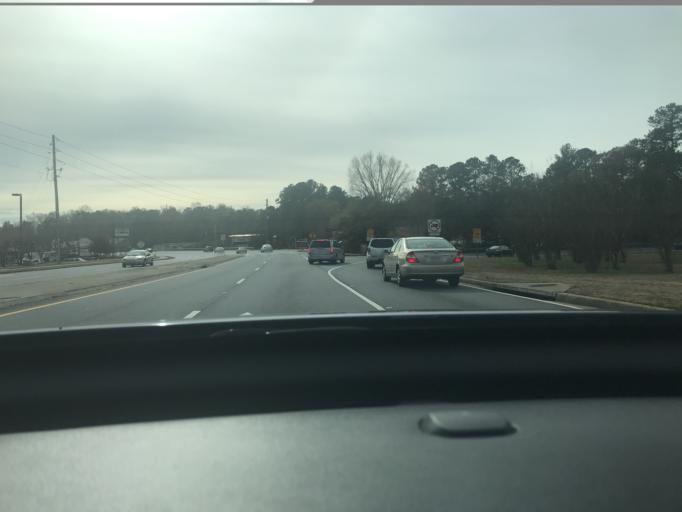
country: US
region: Georgia
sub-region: Gwinnett County
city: Lilburn
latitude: 33.9142
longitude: -84.1142
